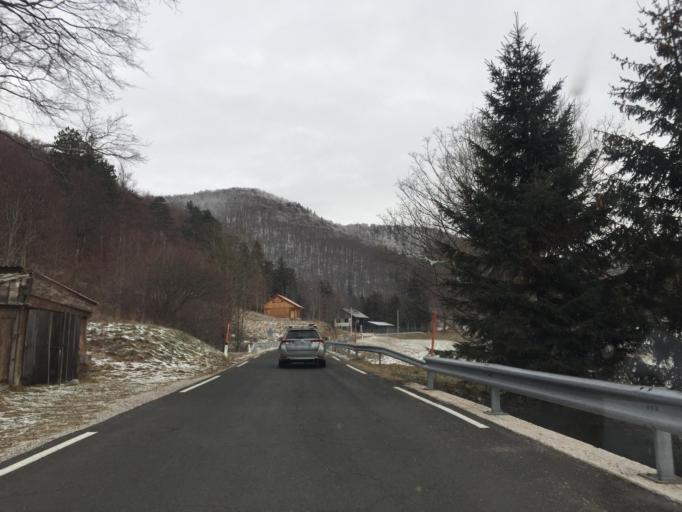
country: SI
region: Nova Gorica
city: Sempas
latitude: 46.0117
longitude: 13.7867
